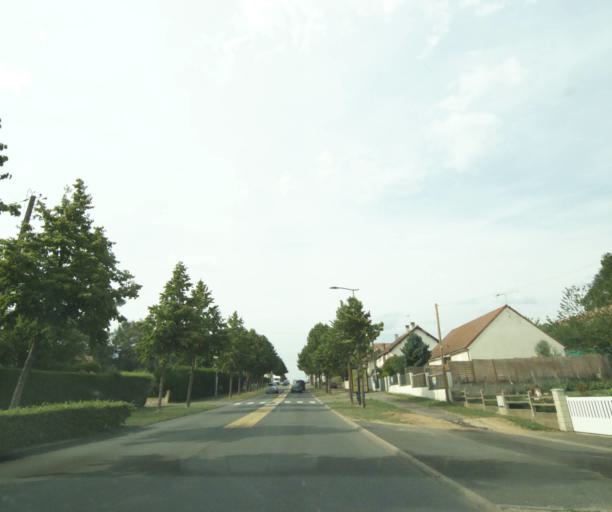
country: FR
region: Pays de la Loire
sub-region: Departement de la Sarthe
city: Mulsanne
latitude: 47.9037
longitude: 0.2449
